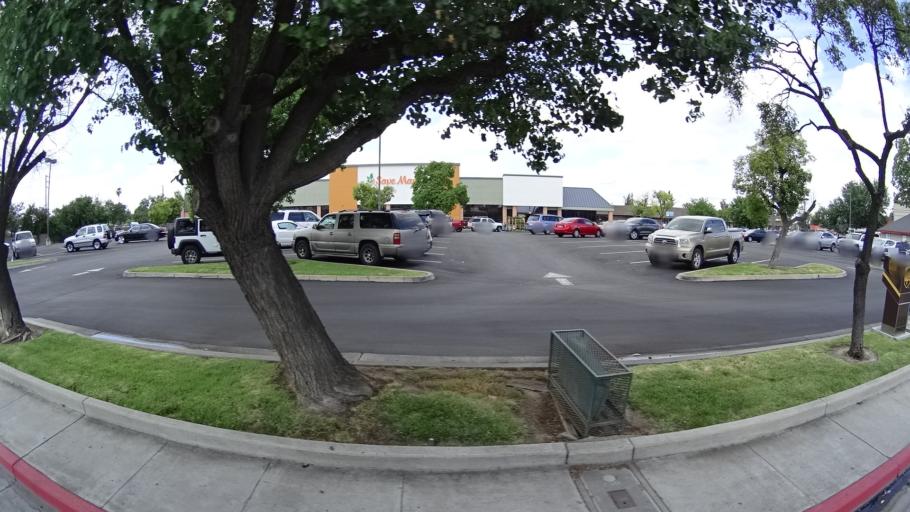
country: US
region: California
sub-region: Kings County
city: Hanford
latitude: 36.3417
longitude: -119.6552
